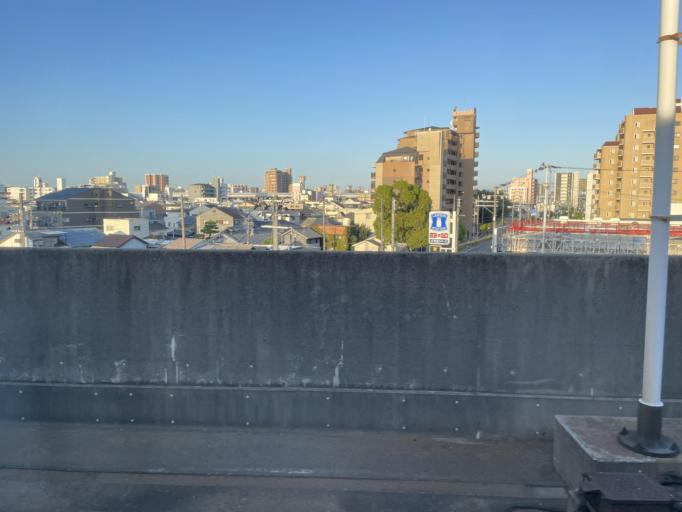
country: JP
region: Osaka
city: Matsubara
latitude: 34.6312
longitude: 135.5293
